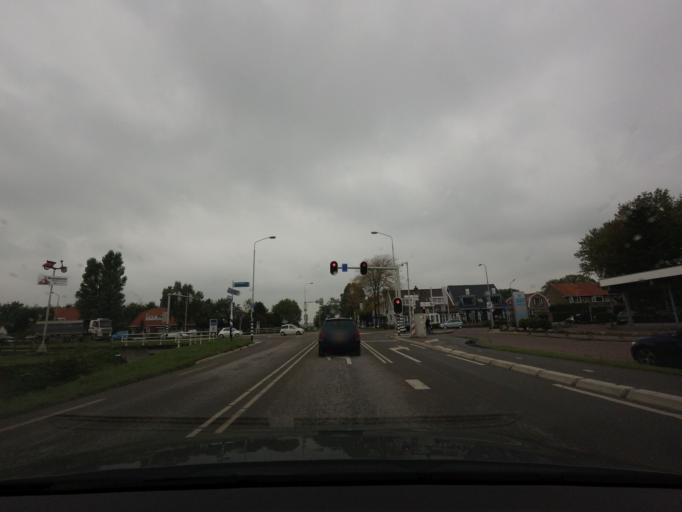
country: NL
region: North Holland
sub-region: Gemeente Aalsmeer
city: Aalsmeer
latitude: 52.3341
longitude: 4.7744
